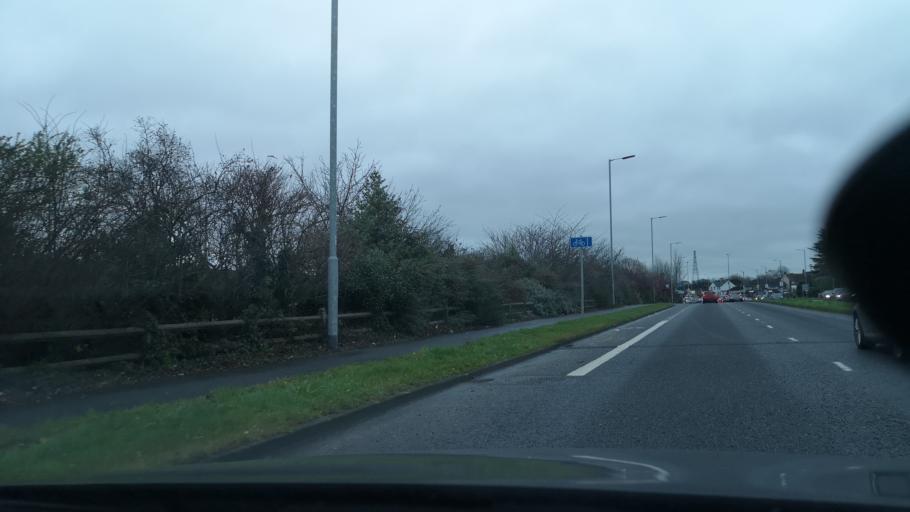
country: GB
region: Northern Ireland
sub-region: Castlereagh District
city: Castlereagh
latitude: 54.5763
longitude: -5.8772
